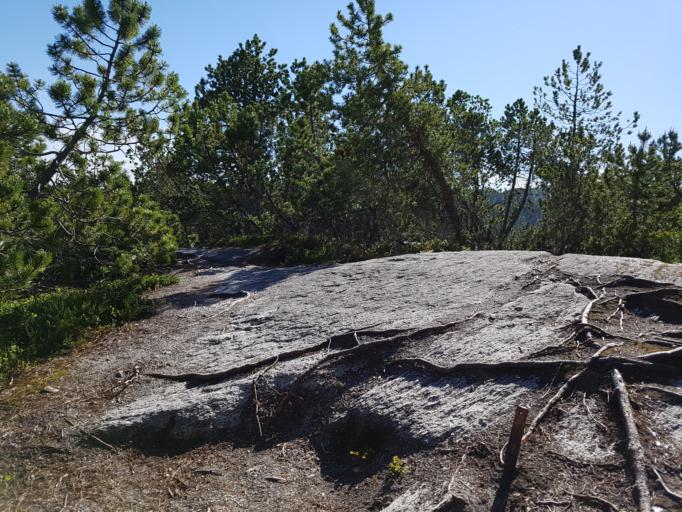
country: NO
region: Sor-Trondelag
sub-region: Trondheim
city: Trondheim
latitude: 63.4302
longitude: 10.2896
